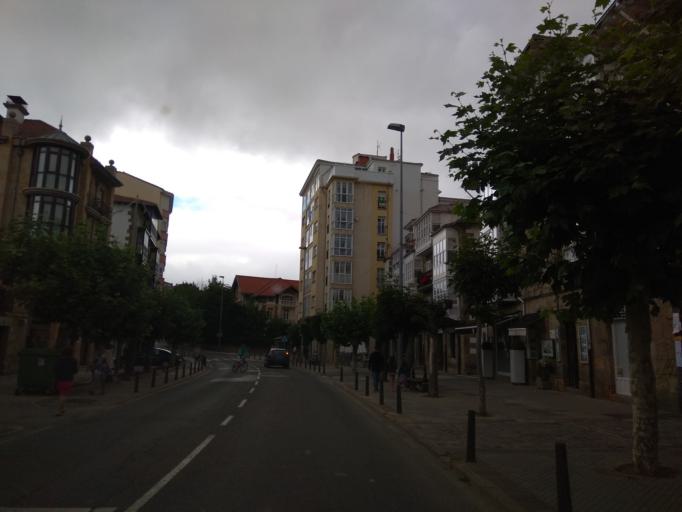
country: ES
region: Cantabria
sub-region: Provincia de Cantabria
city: Reinosa
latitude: 42.9987
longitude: -4.1386
